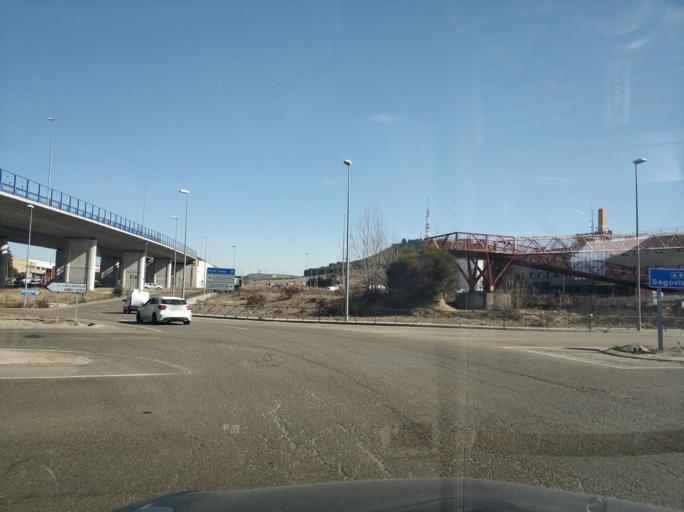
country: ES
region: Castille and Leon
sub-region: Provincia de Valladolid
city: Cisterniga
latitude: 41.6123
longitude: -4.7127
